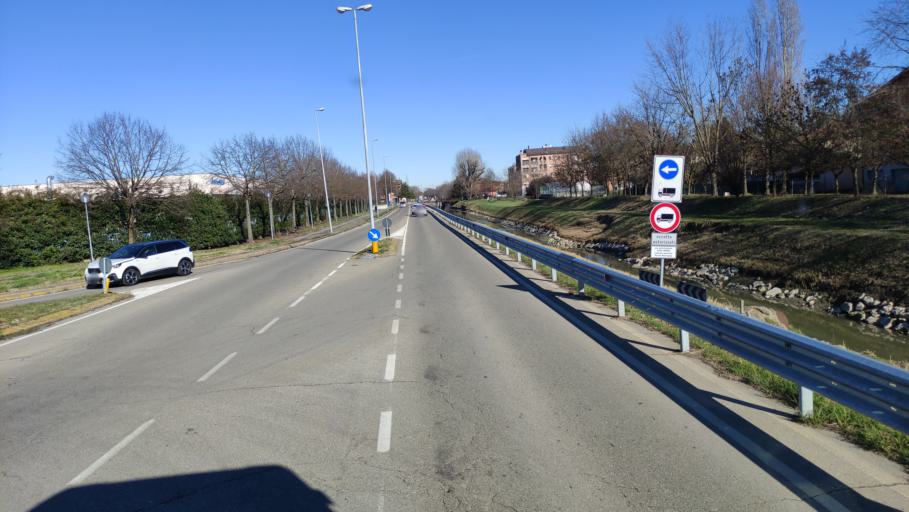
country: IT
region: Emilia-Romagna
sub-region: Provincia di Reggio Emilia
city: San Martino in Rio
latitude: 44.7319
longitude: 10.7794
